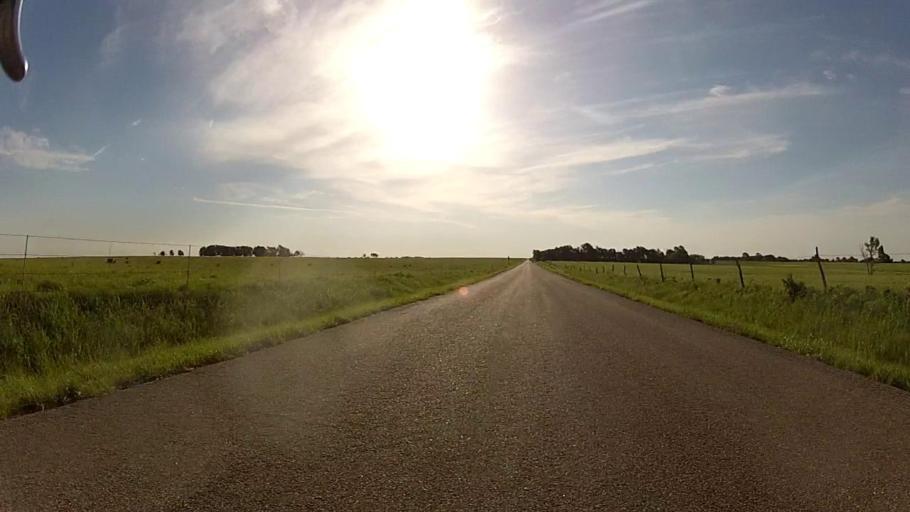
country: US
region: Kansas
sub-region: Cowley County
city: Arkansas City
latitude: 37.0484
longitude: -96.8400
